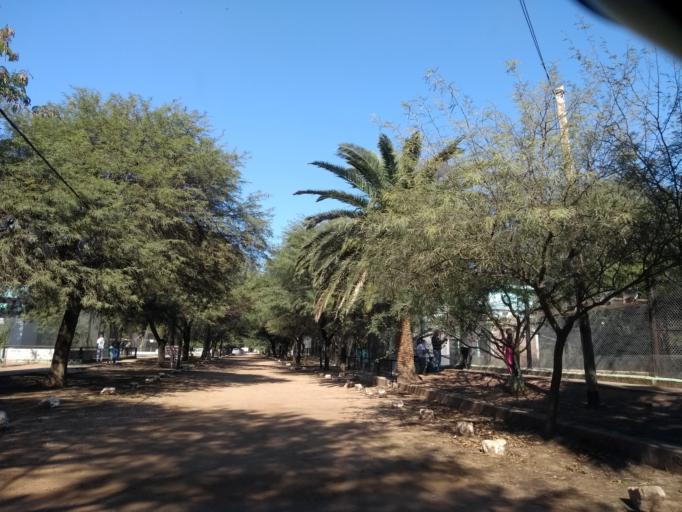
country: AR
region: Chaco
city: Presidencia Roque Saenz Pena
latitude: -26.8177
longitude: -60.4184
